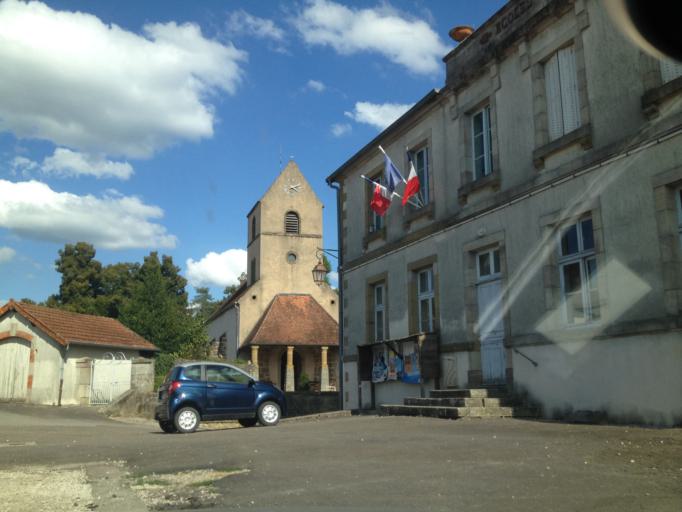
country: FR
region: Franche-Comte
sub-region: Departement de la Haute-Saone
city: Faverney
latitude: 47.8060
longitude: 6.1639
